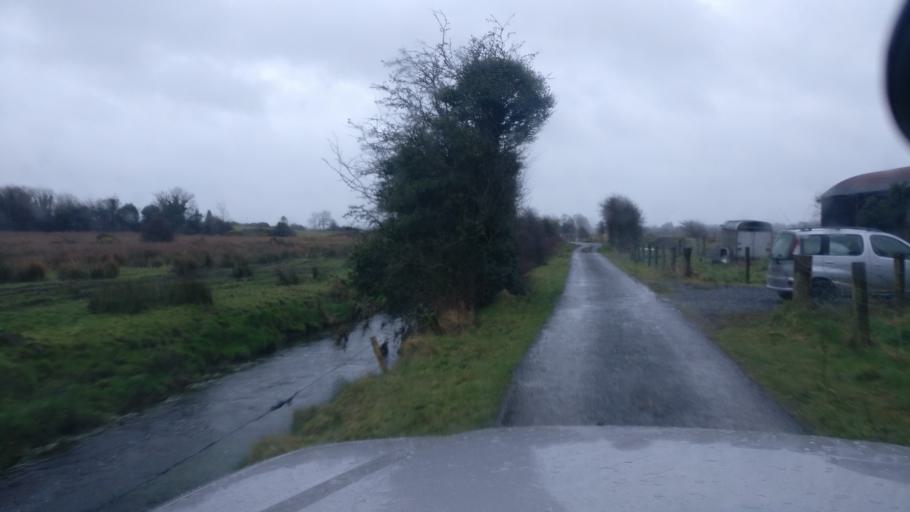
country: IE
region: Connaught
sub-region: County Galway
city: Ballinasloe
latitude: 53.2448
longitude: -8.3429
